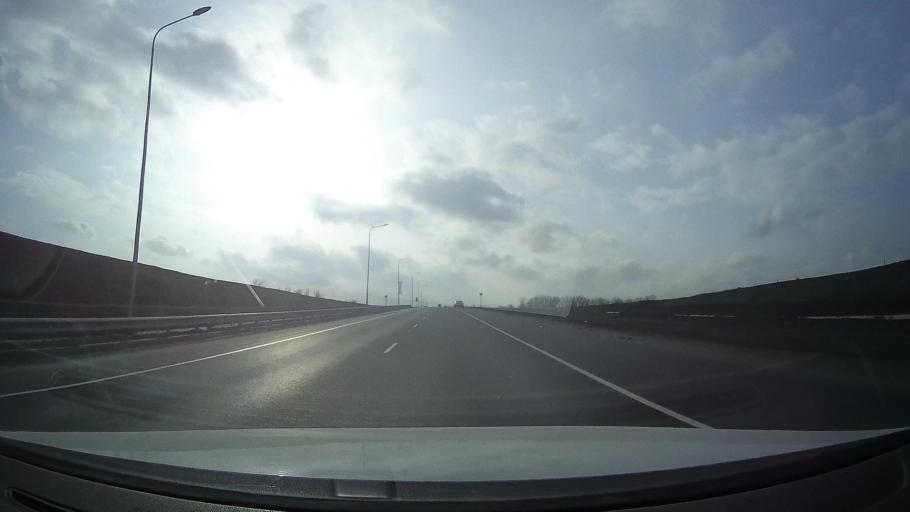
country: RU
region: Rostov
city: Grushevskaya
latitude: 47.4310
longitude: 39.8679
